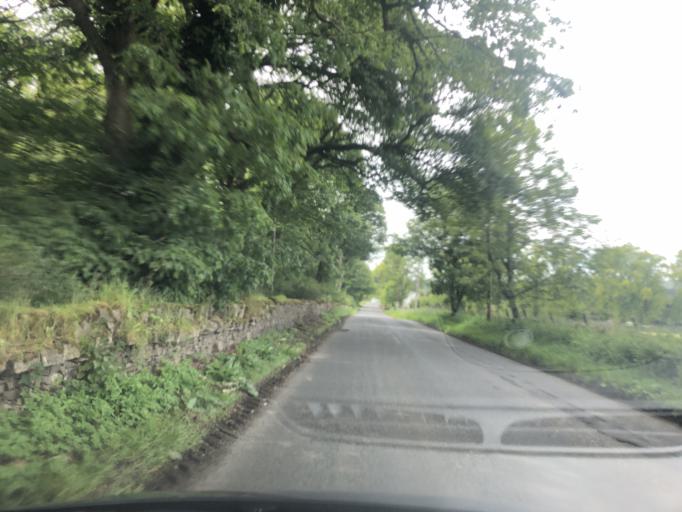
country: GB
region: Scotland
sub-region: The Scottish Borders
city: West Linton
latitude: 55.7431
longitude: -3.3440
